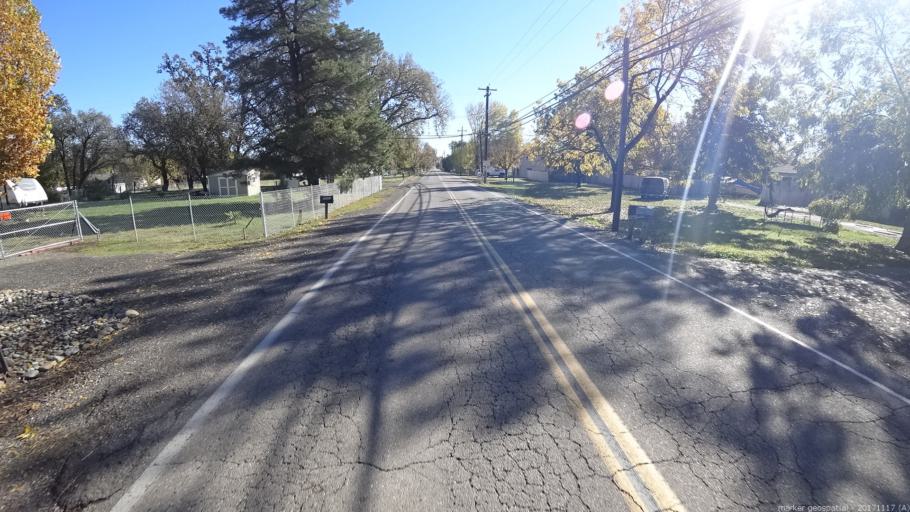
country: US
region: California
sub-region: Shasta County
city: Anderson
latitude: 40.4452
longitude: -122.2524
